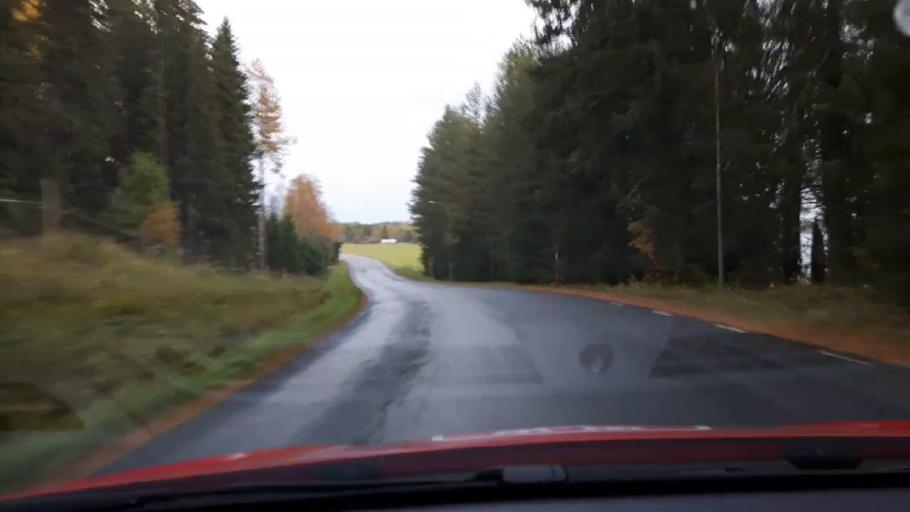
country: SE
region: Jaemtland
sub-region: OEstersunds Kommun
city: Lit
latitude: 63.3168
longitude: 14.9581
